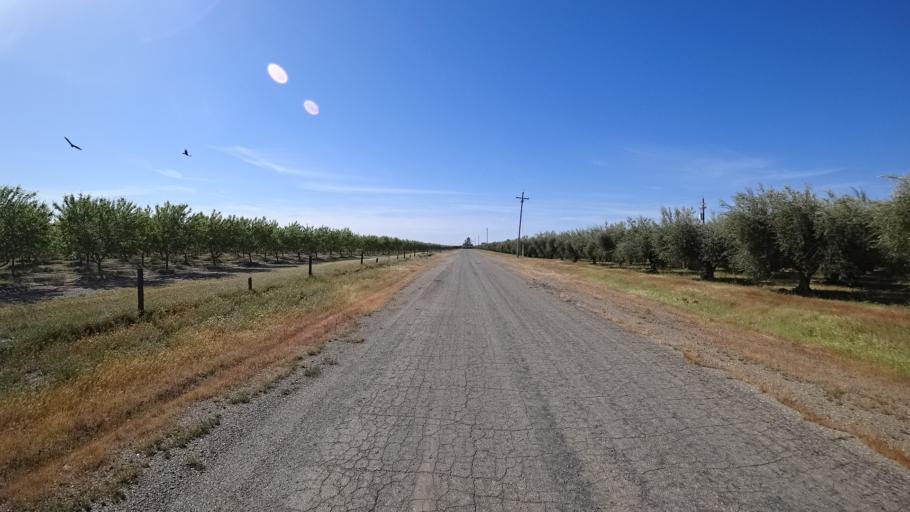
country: US
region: California
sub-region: Glenn County
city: Willows
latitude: 39.6280
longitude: -122.1601
